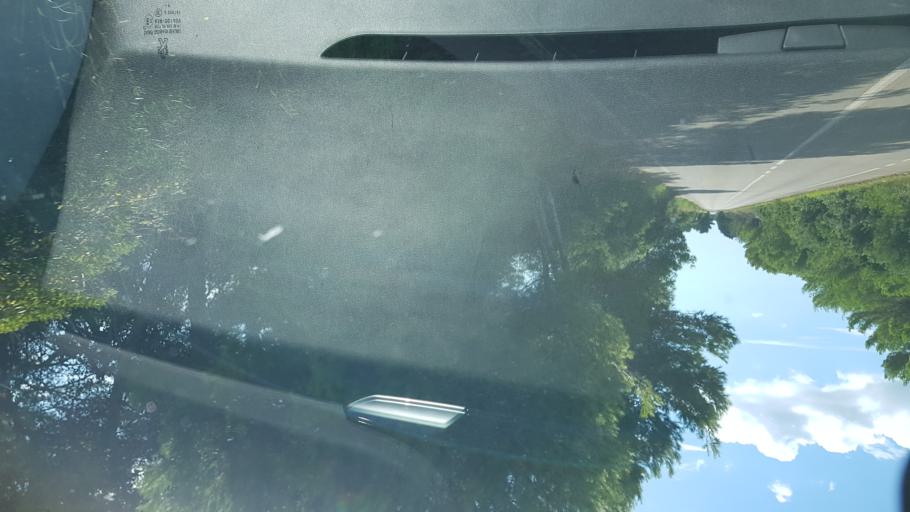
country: IT
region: Apulia
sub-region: Provincia di Lecce
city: Borgagne
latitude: 40.2524
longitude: 18.4393
